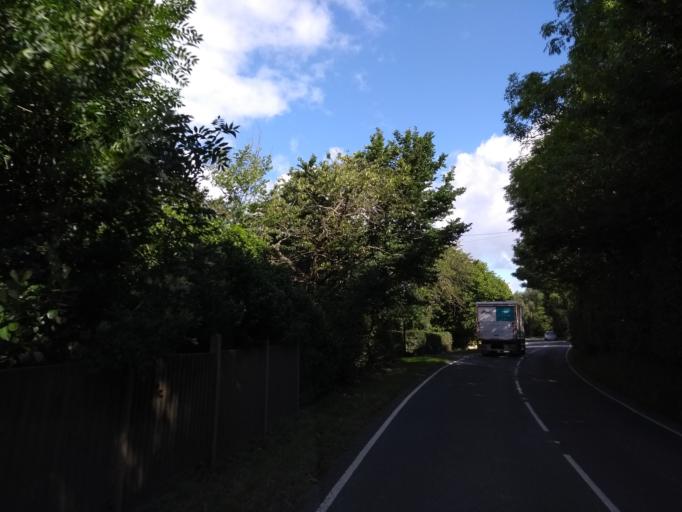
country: GB
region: England
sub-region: Somerset
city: Street
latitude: 51.0758
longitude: -2.7226
